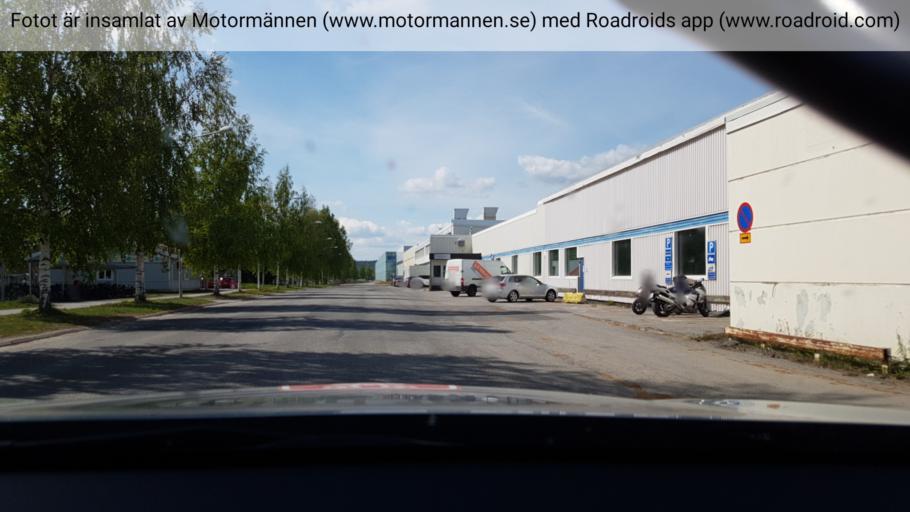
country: SE
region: Vaesterbotten
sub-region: Umea Kommun
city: Umea
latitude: 63.8217
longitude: 20.2228
